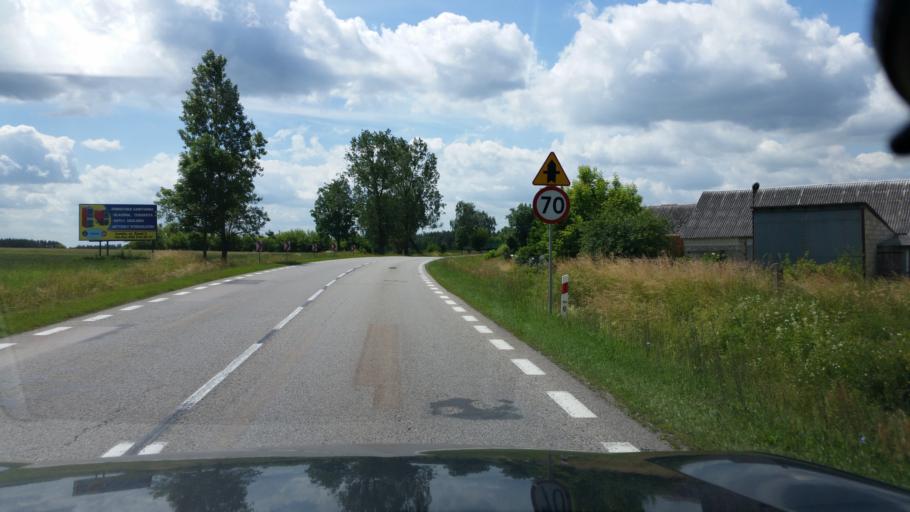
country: PL
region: Podlasie
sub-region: Powiat kolnenski
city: Stawiski
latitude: 53.2943
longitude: 22.1460
